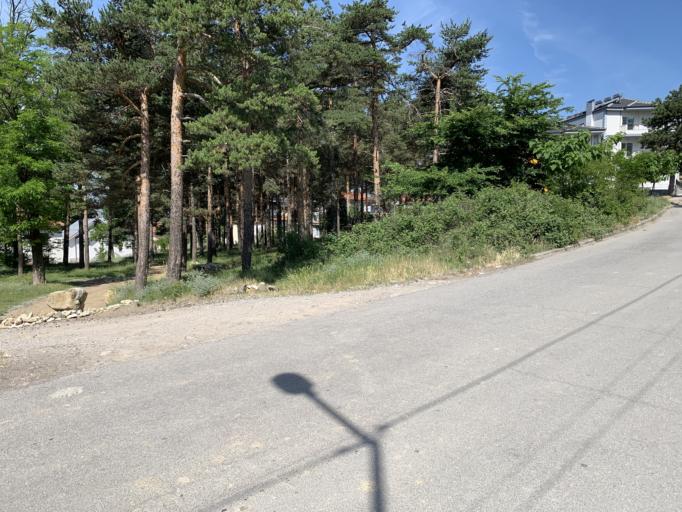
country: AL
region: Korce
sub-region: Rrethi i Korces
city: Korce
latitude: 40.6148
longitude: 20.7887
